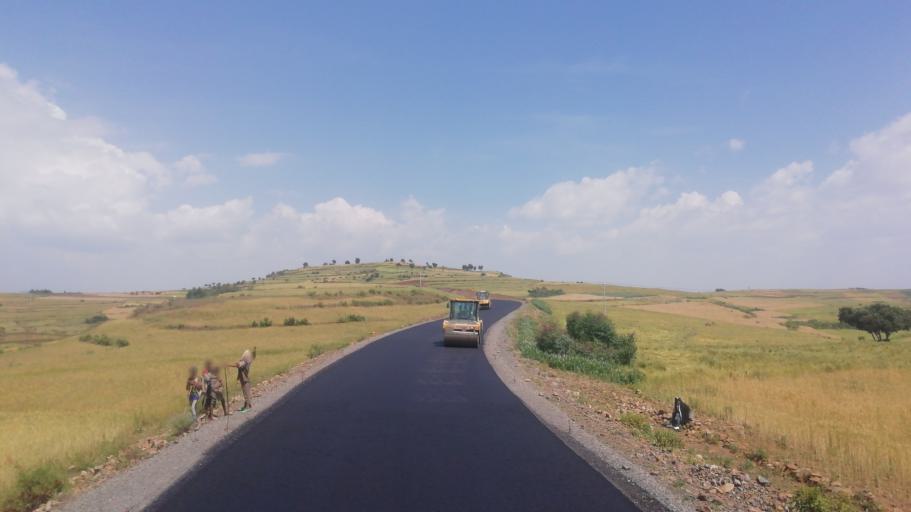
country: ET
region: Amhara
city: Addiet Canna
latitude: 11.3718
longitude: 37.8743
